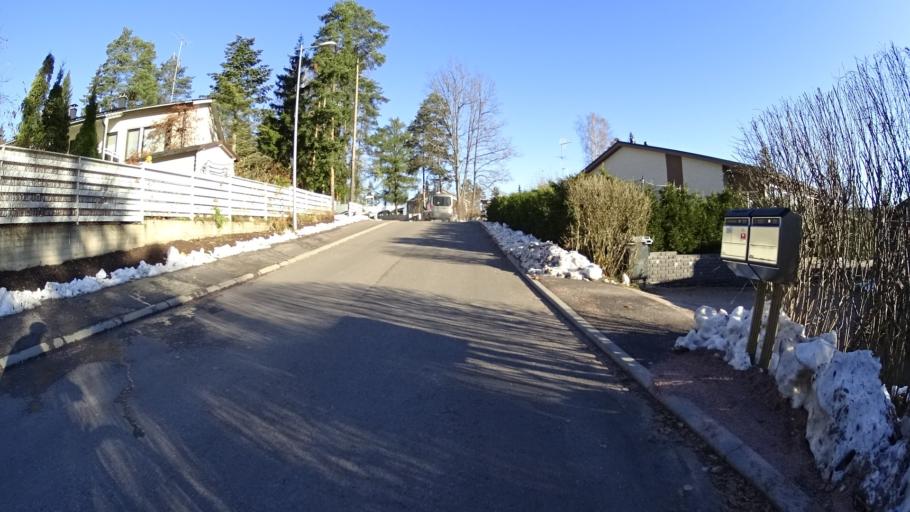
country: FI
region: Uusimaa
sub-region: Helsinki
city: Kauniainen
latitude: 60.2358
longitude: 24.7519
